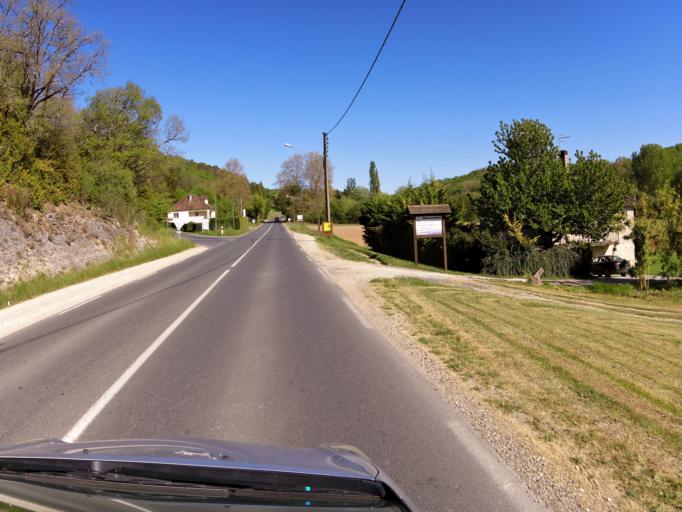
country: FR
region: Aquitaine
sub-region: Departement de la Dordogne
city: Montignac
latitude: 45.0635
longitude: 1.1798
